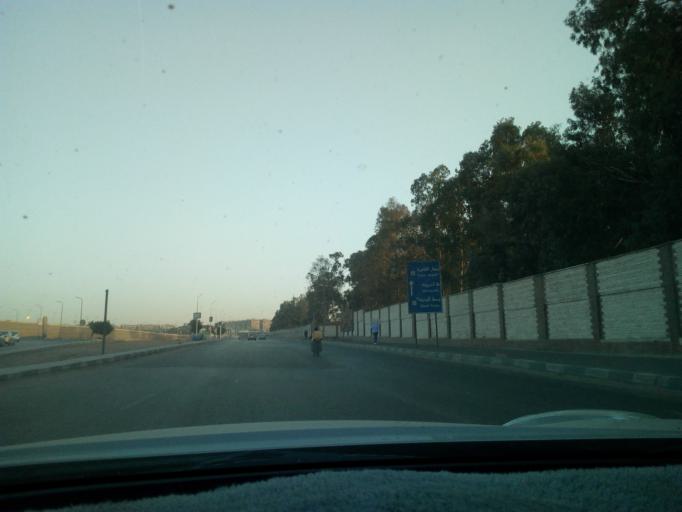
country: EG
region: Muhafazat al Qalyubiyah
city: Al Khankah
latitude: 30.1163
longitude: 31.3644
